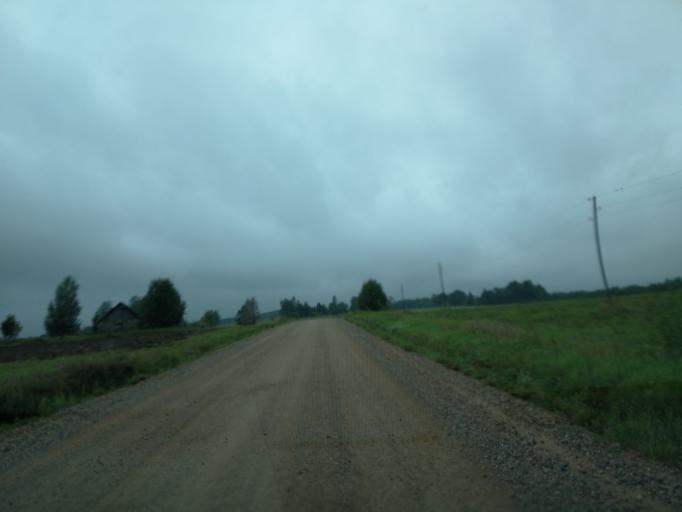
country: LV
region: Vilanu
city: Vilani
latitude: 56.3731
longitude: 27.0372
